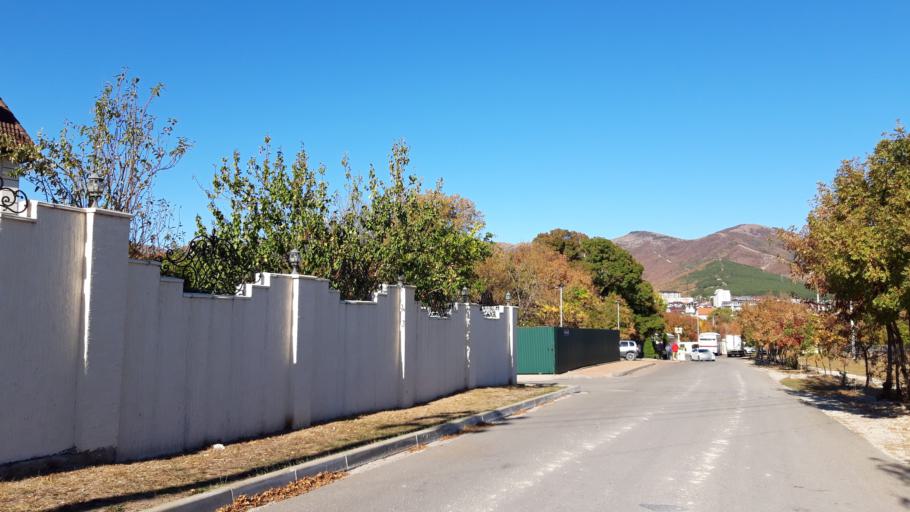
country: RU
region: Krasnodarskiy
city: Kabardinka
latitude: 44.6432
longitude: 37.9354
